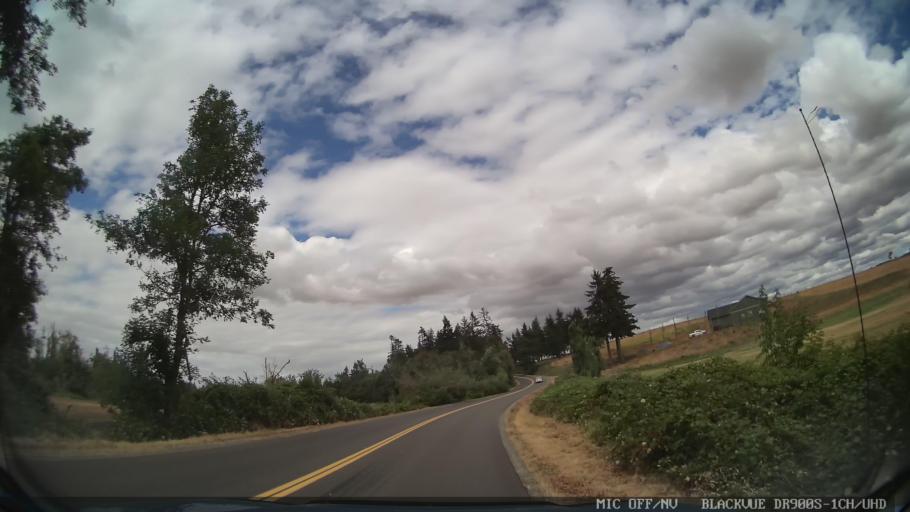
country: US
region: Oregon
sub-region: Marion County
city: Aumsville
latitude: 44.8624
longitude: -122.8506
